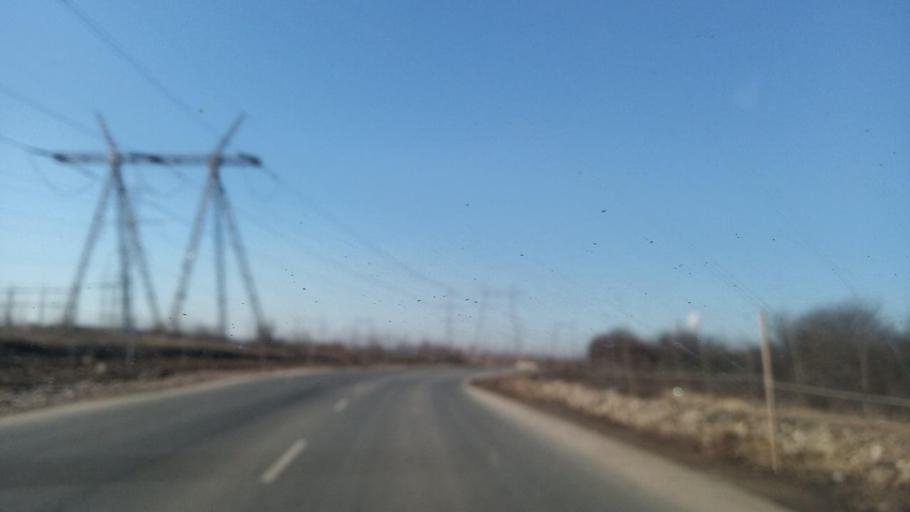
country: RO
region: Ilfov
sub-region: Comuna Popesti-Leordeni
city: Popesti-Leordeni
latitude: 44.3975
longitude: 26.1859
